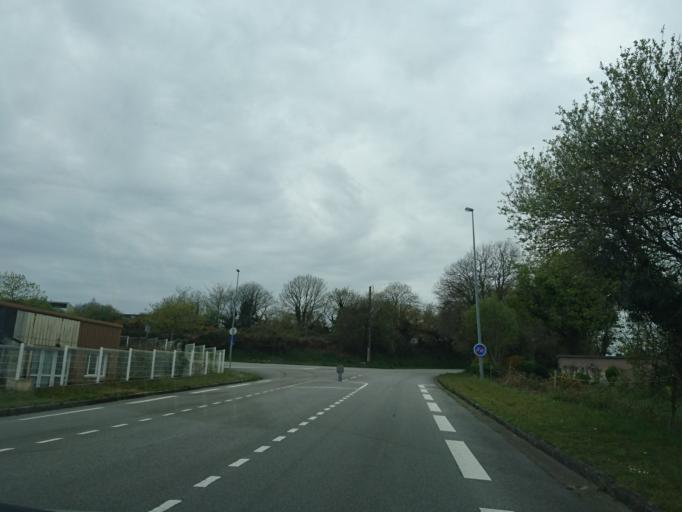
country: FR
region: Brittany
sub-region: Departement du Finistere
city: Roscanvel
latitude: 48.3625
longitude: -4.5694
